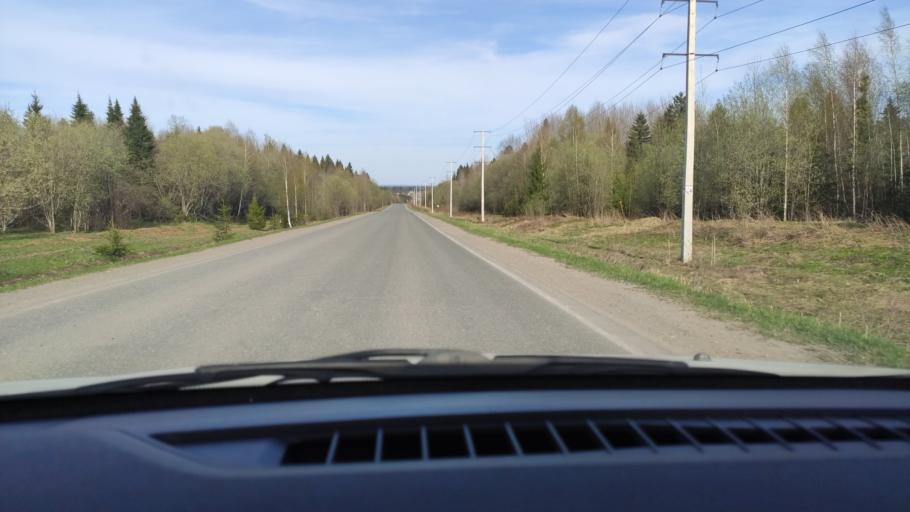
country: RU
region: Perm
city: Novyye Lyady
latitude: 57.9399
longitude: 56.5979
